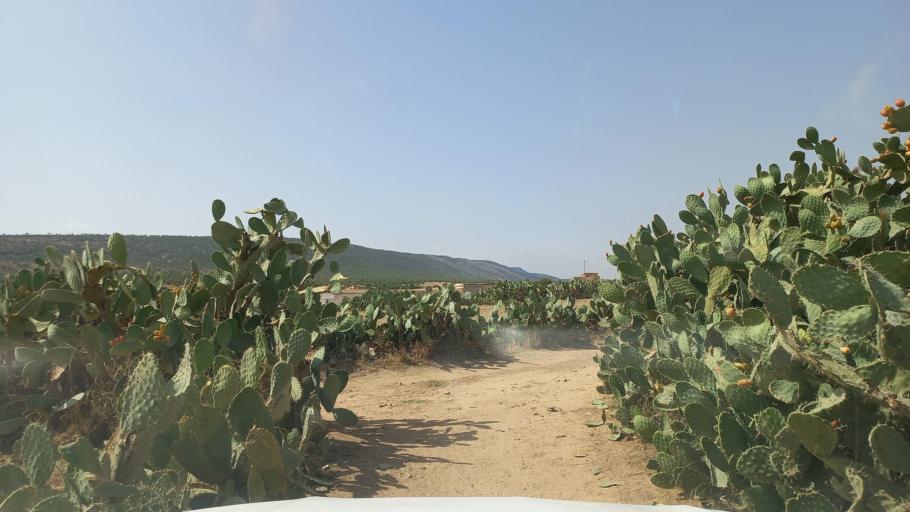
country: TN
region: Al Qasrayn
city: Sbiba
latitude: 35.3864
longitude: 8.9619
